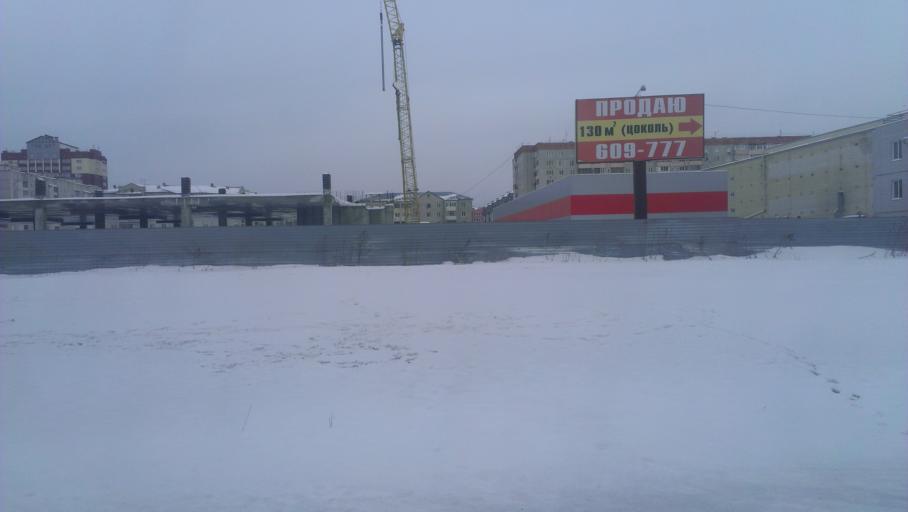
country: RU
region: Altai Krai
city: Novosilikatnyy
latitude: 53.3294
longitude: 83.6719
